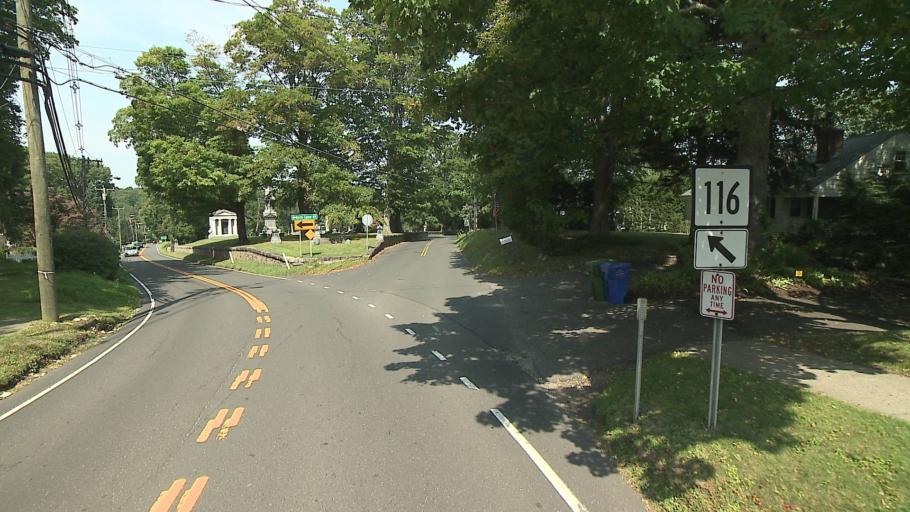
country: US
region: Connecticut
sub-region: Fairfield County
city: Ridgefield
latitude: 41.2904
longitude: -73.5005
